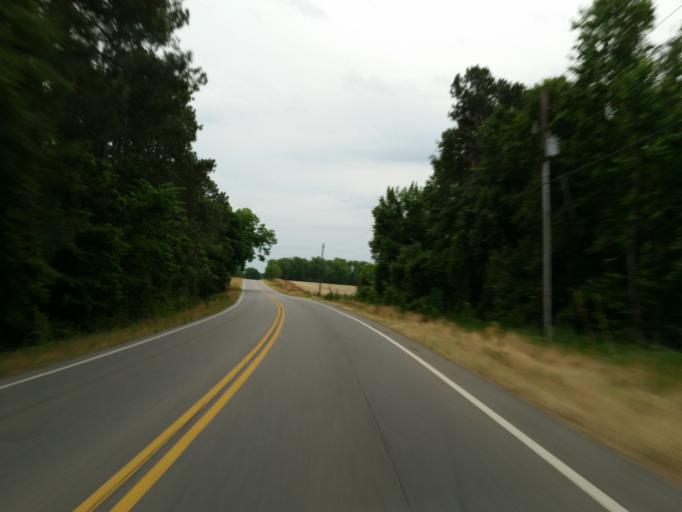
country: US
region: Georgia
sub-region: Dooly County
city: Vienna
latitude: 32.0668
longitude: -83.7988
